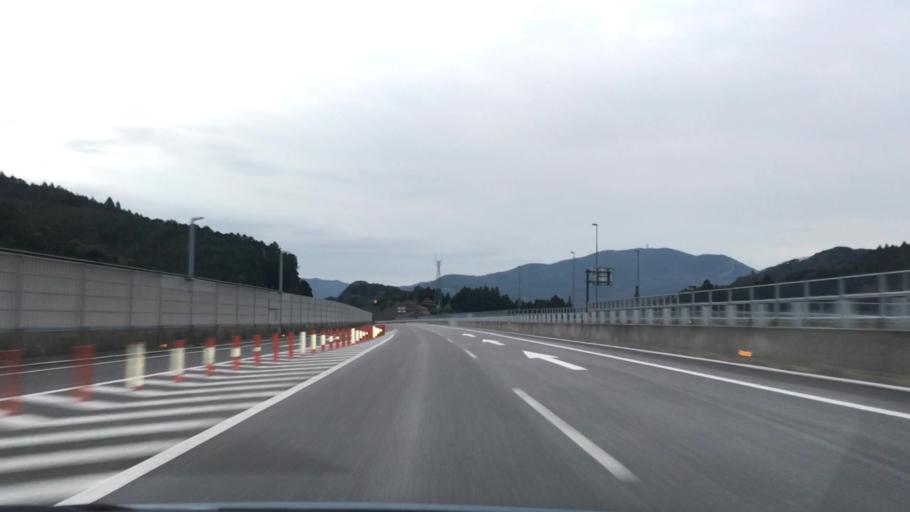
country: JP
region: Aichi
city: Shinshiro
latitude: 34.8723
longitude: 137.6427
